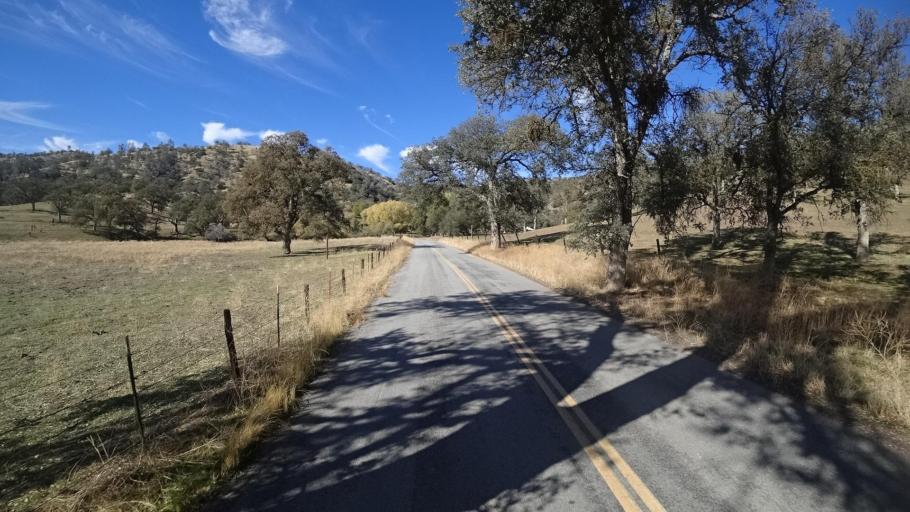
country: US
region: California
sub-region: Kern County
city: Alta Sierra
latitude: 35.6311
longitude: -118.7516
